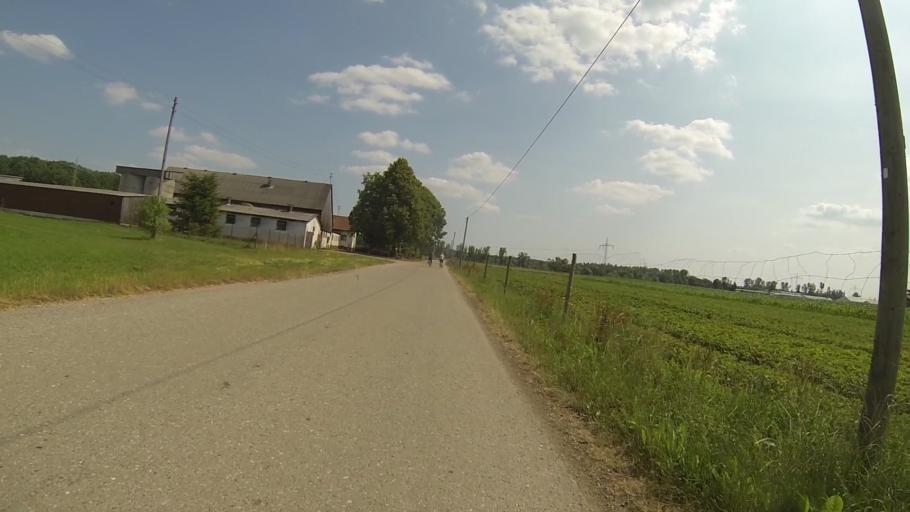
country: DE
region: Bavaria
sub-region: Swabia
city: Guenzburg
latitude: 48.4841
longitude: 10.2884
